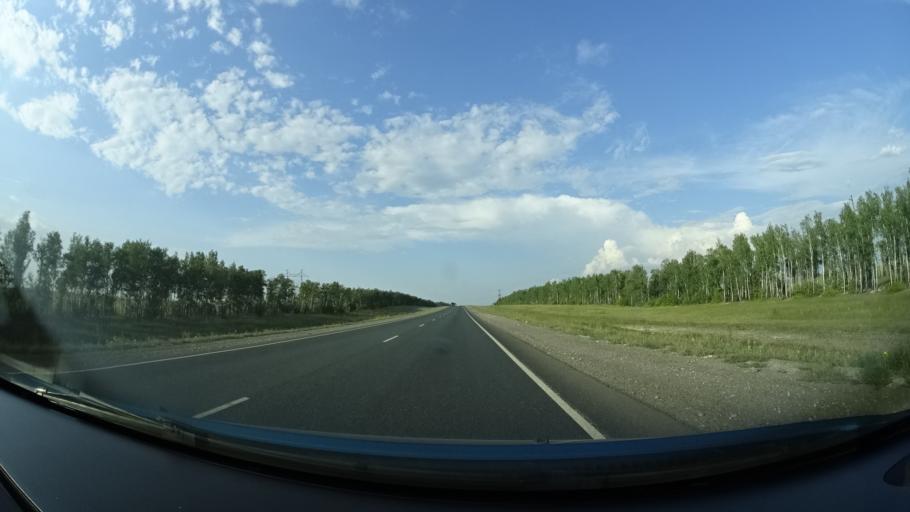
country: RU
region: Samara
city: Sukhodol
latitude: 53.7118
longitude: 50.8172
